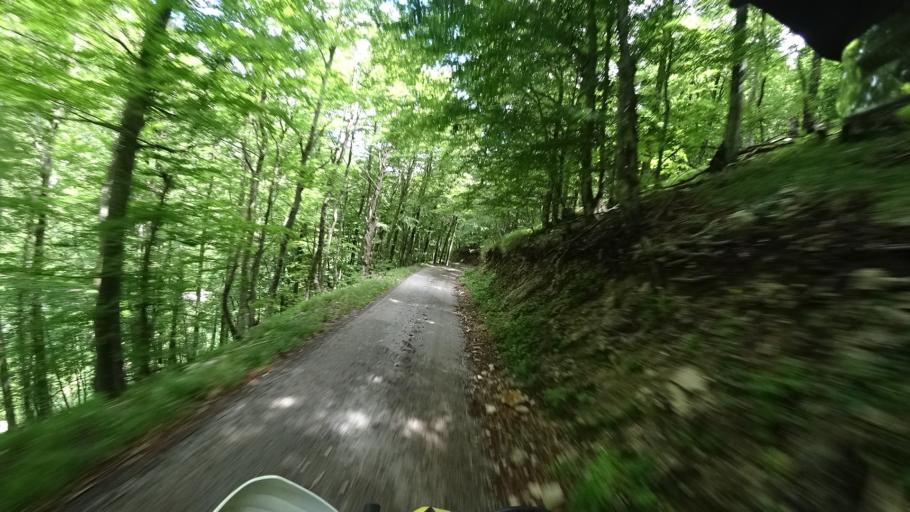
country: HR
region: Primorsko-Goranska
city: Bribir
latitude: 45.2454
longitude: 14.7730
